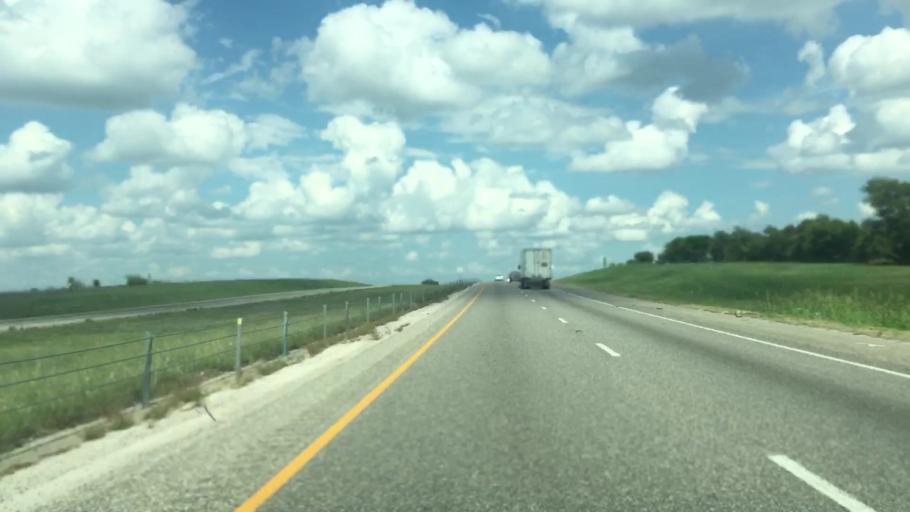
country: US
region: Texas
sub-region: Ellis County
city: Plum Grove
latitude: 32.1111
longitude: -96.9987
